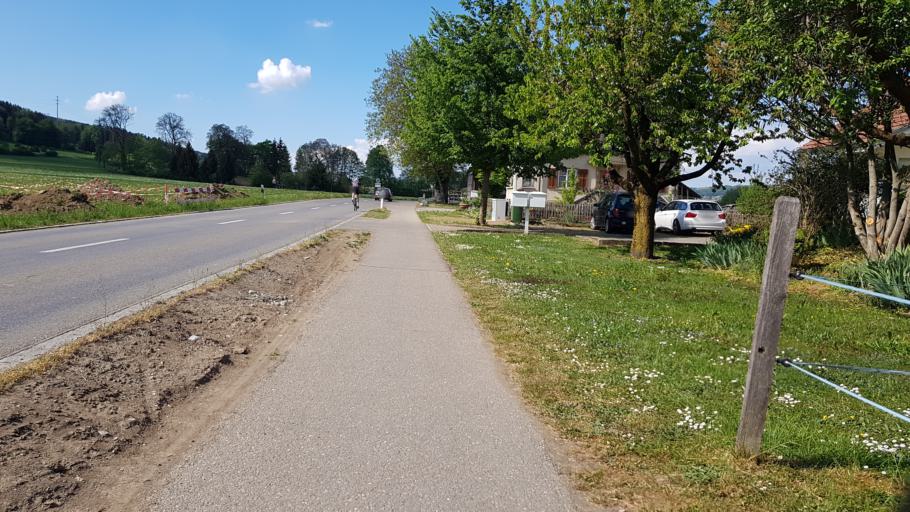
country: CH
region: Lucerne
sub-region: Hochdorf District
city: Hitzkirch
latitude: 47.2116
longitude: 8.2424
